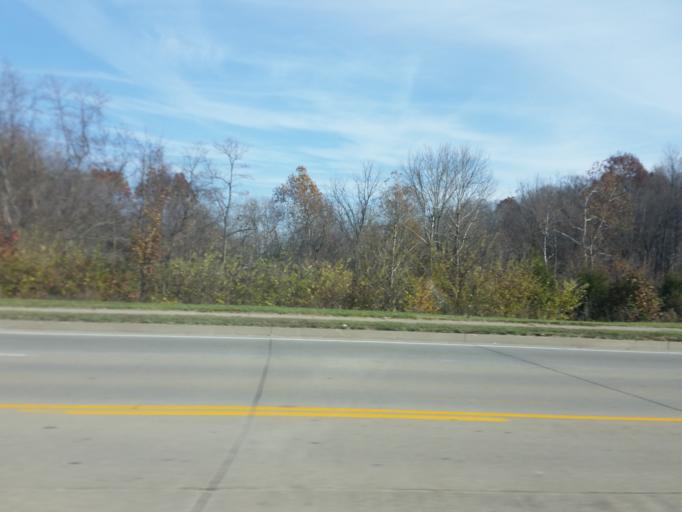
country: US
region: Kentucky
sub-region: Campbell County
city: Alexandria
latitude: 38.9525
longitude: -84.3935
